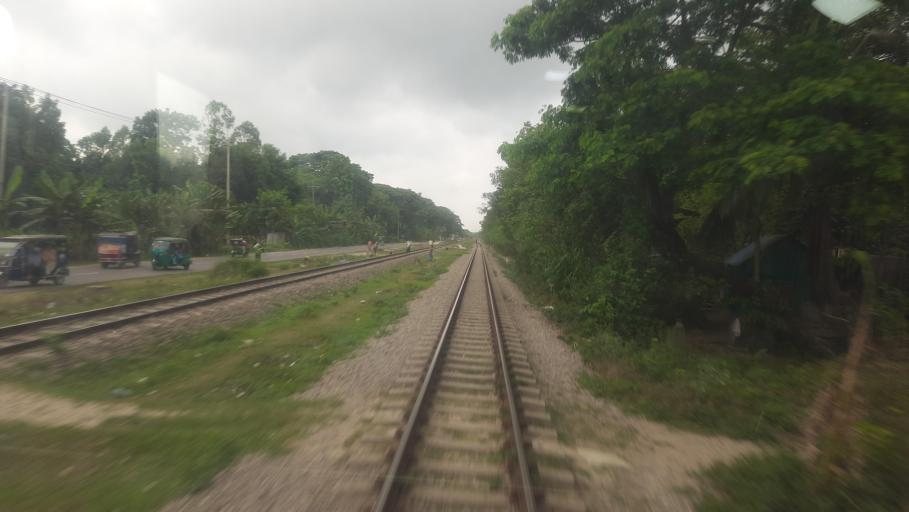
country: BD
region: Dhaka
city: Narsingdi
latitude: 23.9689
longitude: 90.8229
